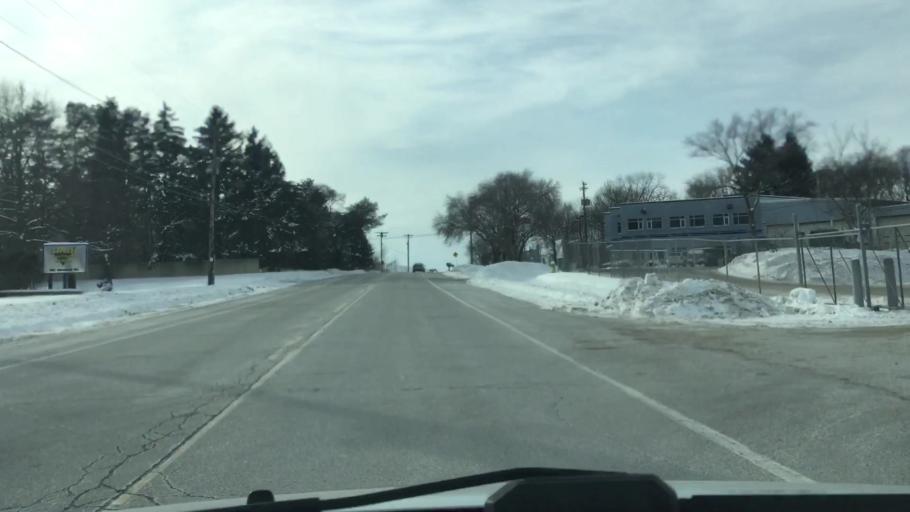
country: US
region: Wisconsin
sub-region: Waukesha County
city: Waukesha
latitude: 43.0456
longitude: -88.2392
